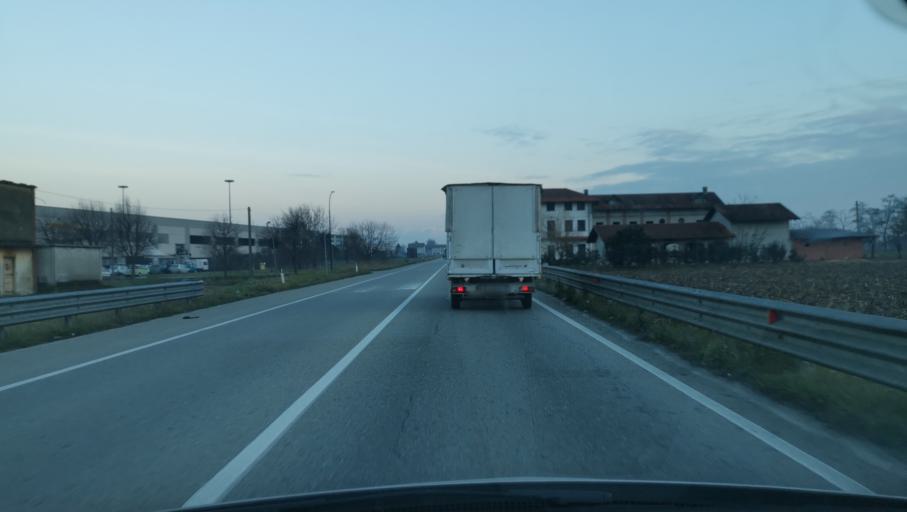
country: IT
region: Piedmont
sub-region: Provincia di Torino
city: Chivasso
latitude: 45.2141
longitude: 7.8903
